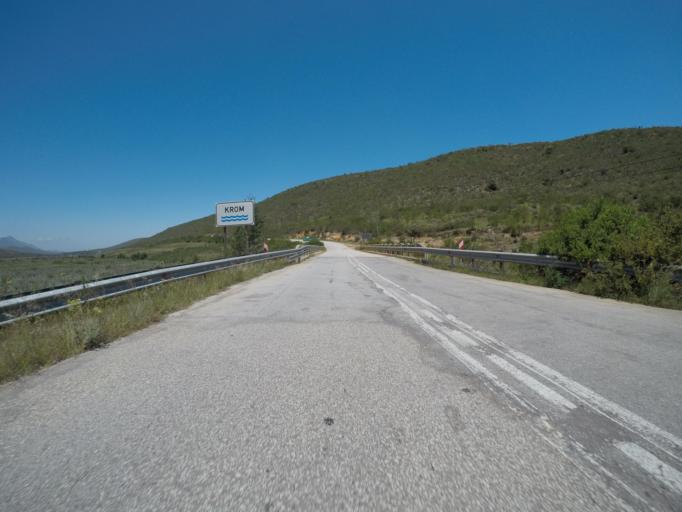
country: ZA
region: Eastern Cape
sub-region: Cacadu District Municipality
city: Kareedouw
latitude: -33.8781
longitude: 24.0531
